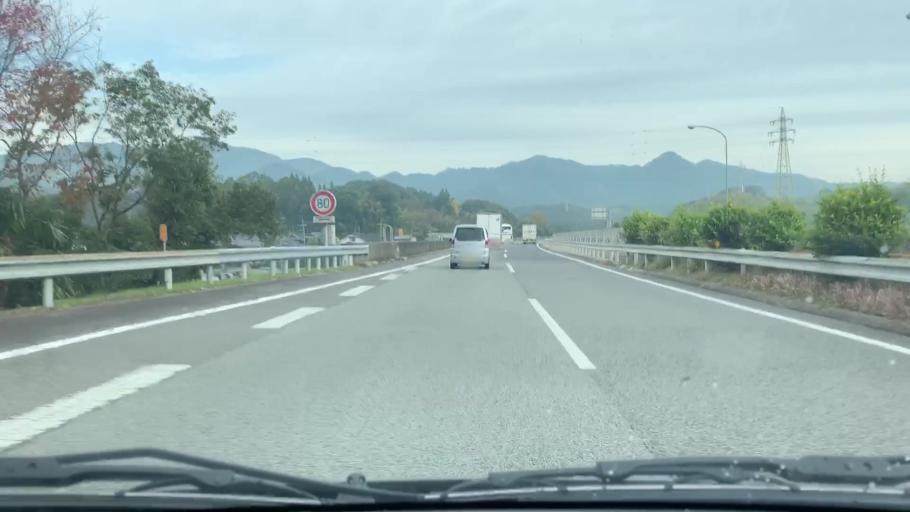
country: JP
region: Saga Prefecture
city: Takeocho-takeo
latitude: 33.2217
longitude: 130.0496
